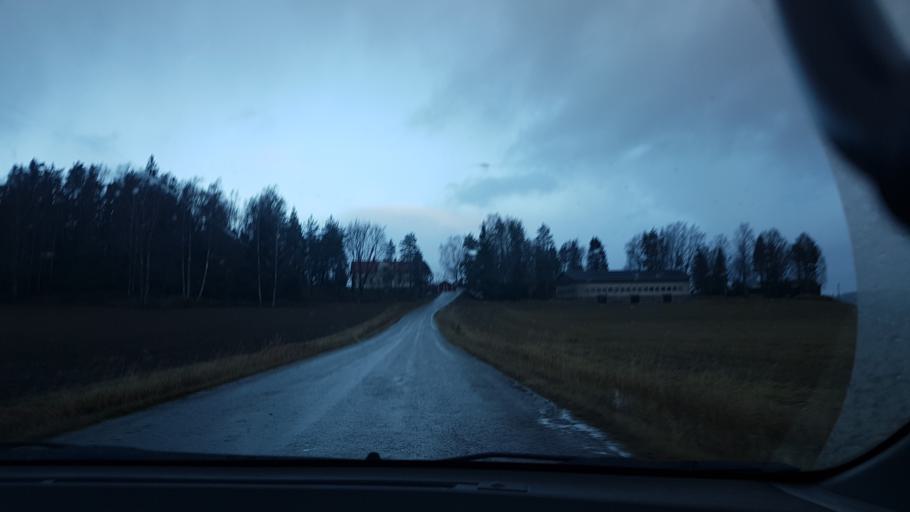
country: FI
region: Uusimaa
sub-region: Helsinki
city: Lohja
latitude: 60.2104
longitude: 24.1009
